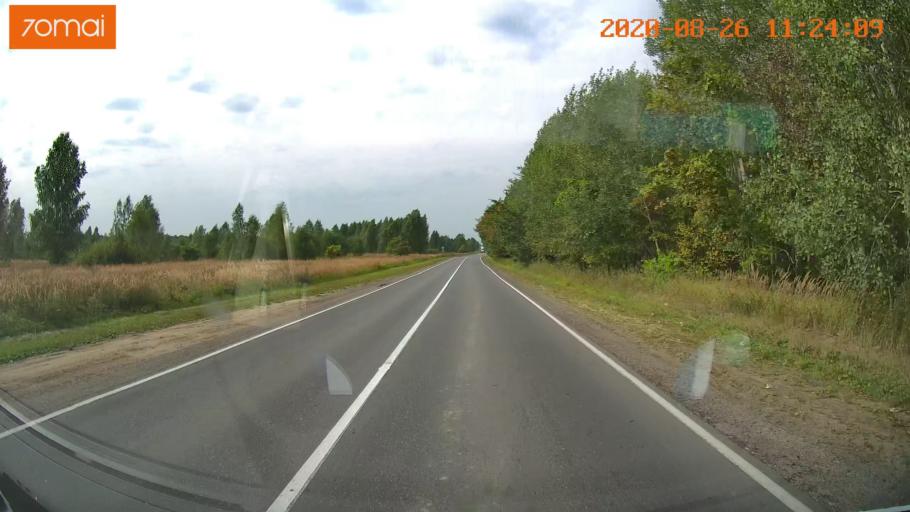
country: RU
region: Rjazan
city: Shilovo
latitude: 54.3481
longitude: 40.9940
